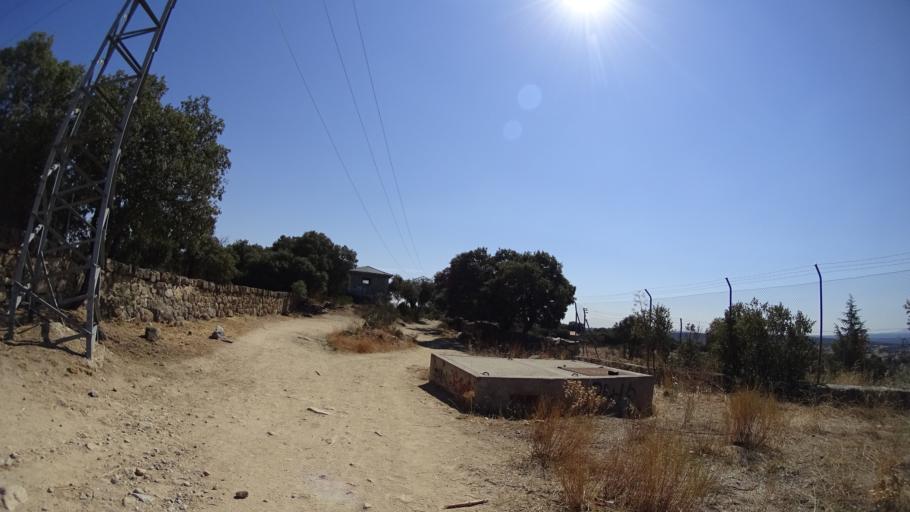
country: ES
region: Madrid
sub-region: Provincia de Madrid
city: Galapagar
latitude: 40.6050
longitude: -4.0111
